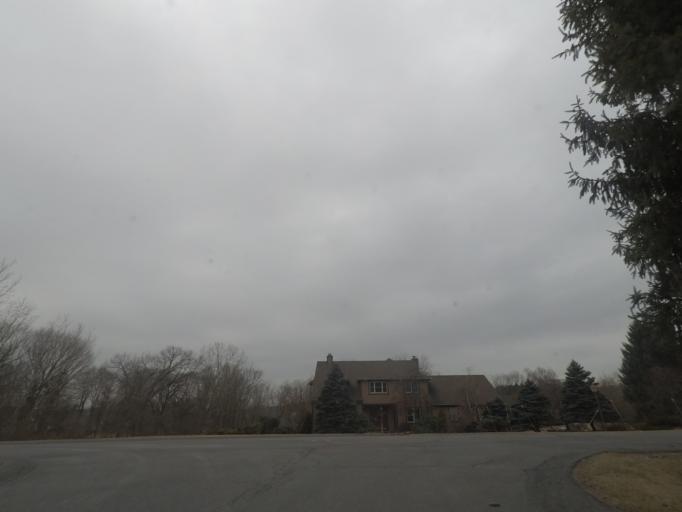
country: US
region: New York
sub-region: Rensselaer County
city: East Greenbush
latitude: 42.5633
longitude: -73.6505
